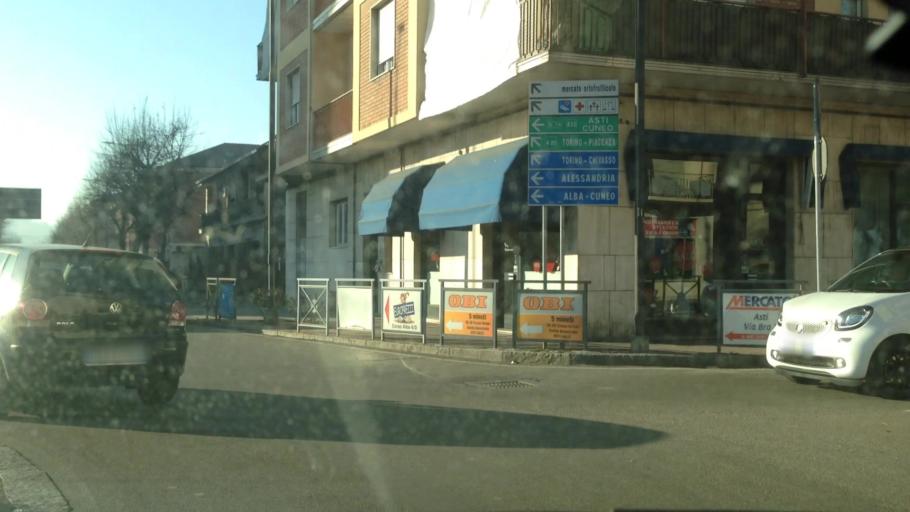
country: IT
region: Piedmont
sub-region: Provincia di Asti
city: Asti
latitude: 44.8923
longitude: 8.2105
